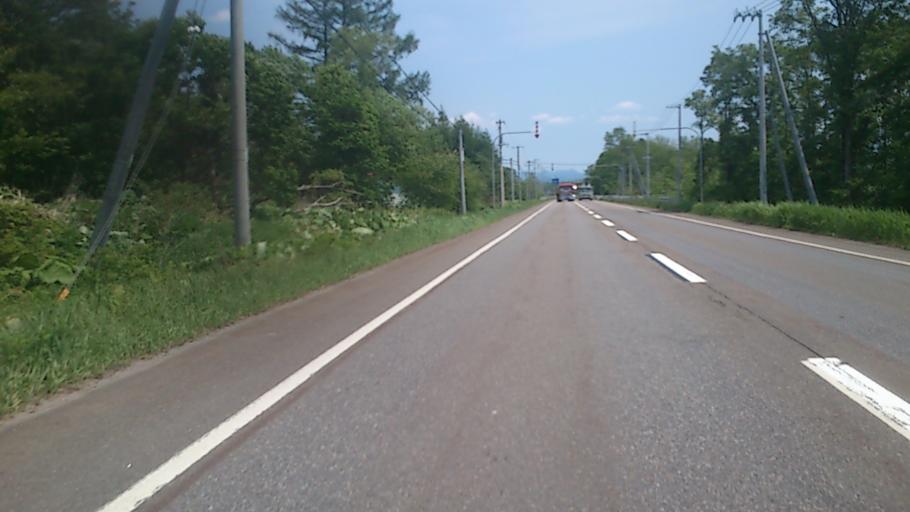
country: JP
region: Hokkaido
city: Otofuke
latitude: 43.2299
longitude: 143.5167
